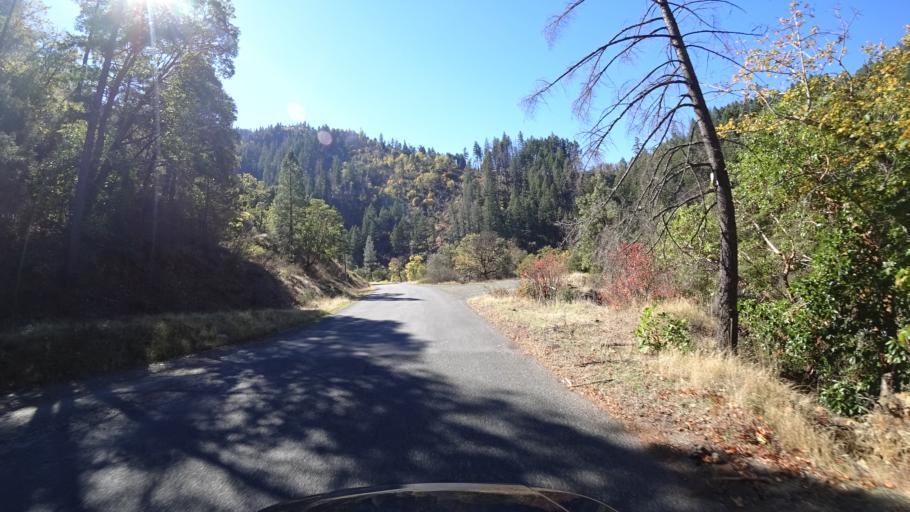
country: US
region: California
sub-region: Humboldt County
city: Willow Creek
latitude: 41.2893
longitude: -123.3640
